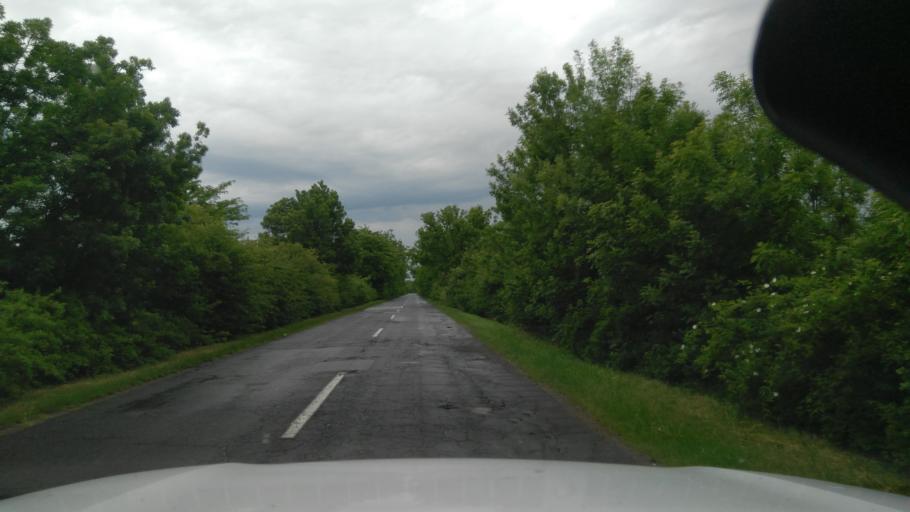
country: HU
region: Bekes
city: Bekescsaba
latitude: 46.6922
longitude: 21.1691
